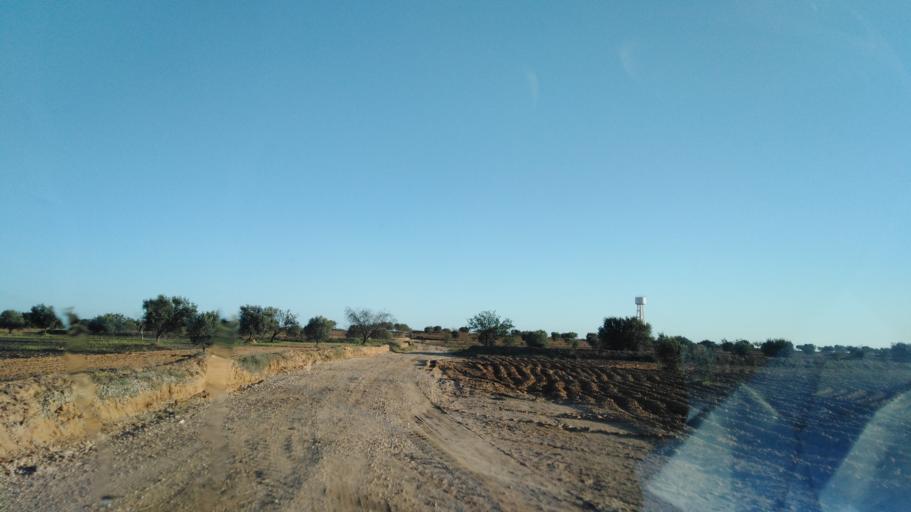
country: TN
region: Safaqis
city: Bi'r `Ali Bin Khalifah
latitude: 34.6736
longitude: 10.3831
